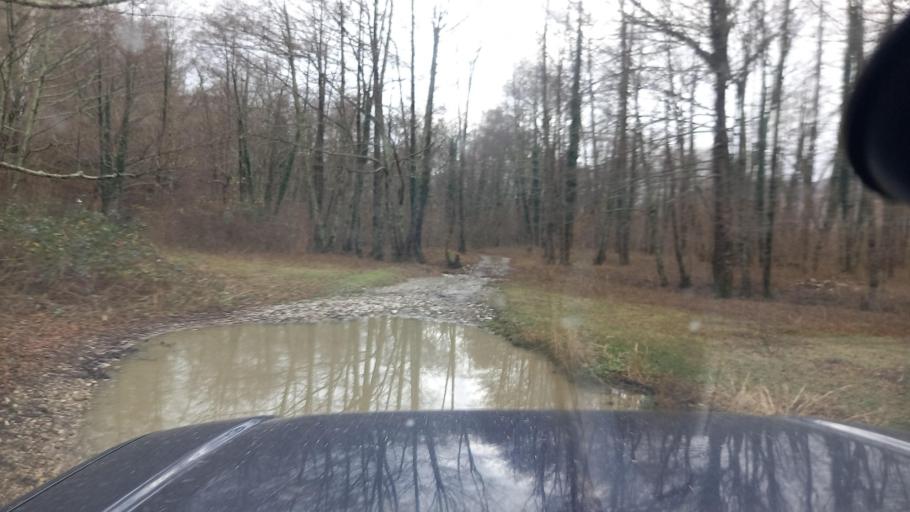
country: RU
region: Krasnodarskiy
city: Pshada
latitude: 44.4879
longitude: 38.4137
